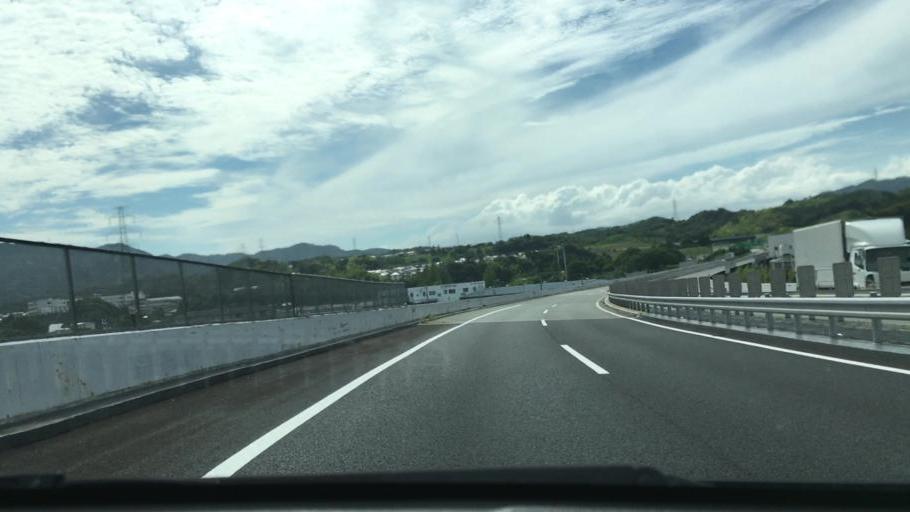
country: JP
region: Yamaguchi
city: Ogori-shimogo
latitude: 34.1229
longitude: 131.4130
